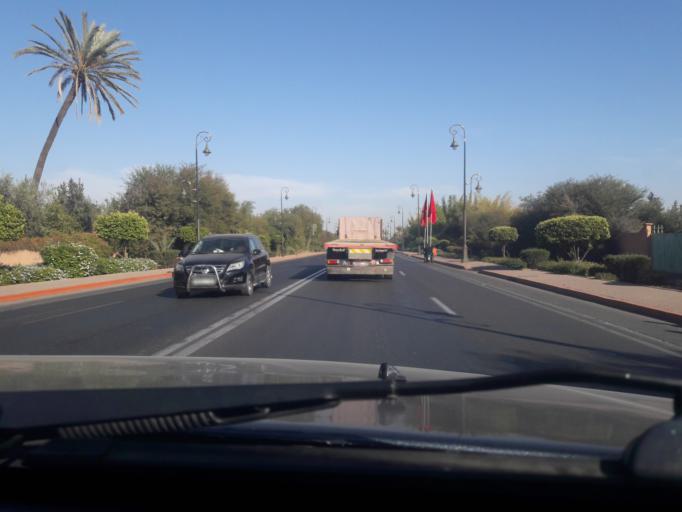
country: MA
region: Marrakech-Tensift-Al Haouz
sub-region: Marrakech
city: Marrakesh
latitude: 31.6469
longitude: -7.9722
